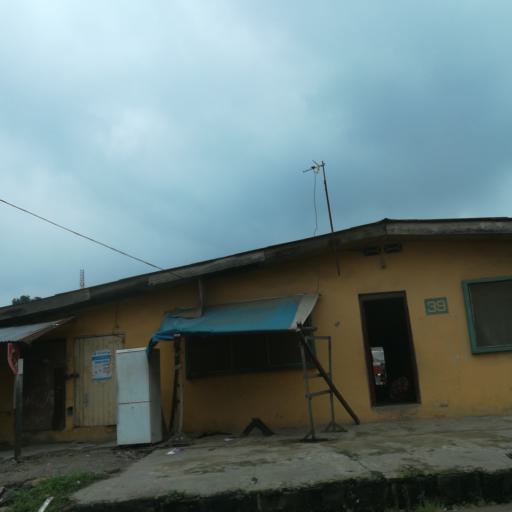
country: NG
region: Lagos
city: Agege
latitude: 6.5968
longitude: 3.2997
